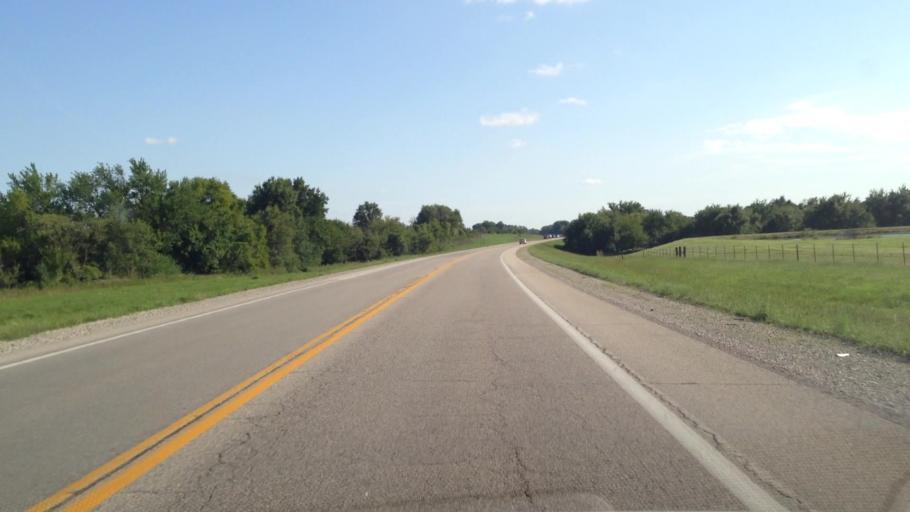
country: US
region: Kansas
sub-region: Crawford County
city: Arma
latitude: 37.5385
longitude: -94.7097
